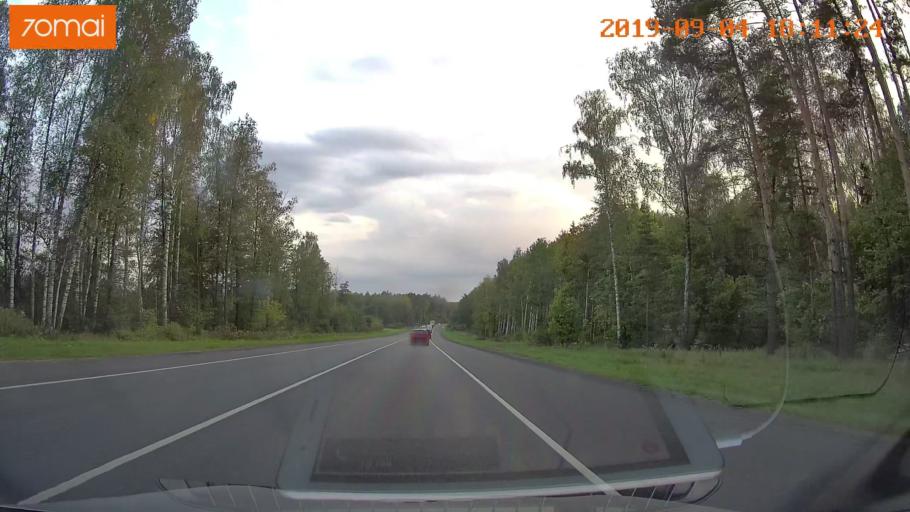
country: RU
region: Moskovskaya
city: Lopatinskiy
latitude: 55.3784
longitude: 38.7549
